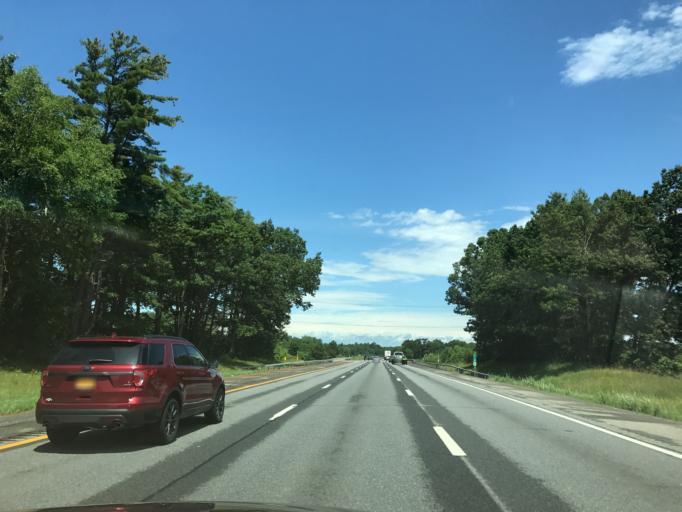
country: US
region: New York
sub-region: Saratoga County
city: Country Knolls
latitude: 42.9352
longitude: -73.8038
